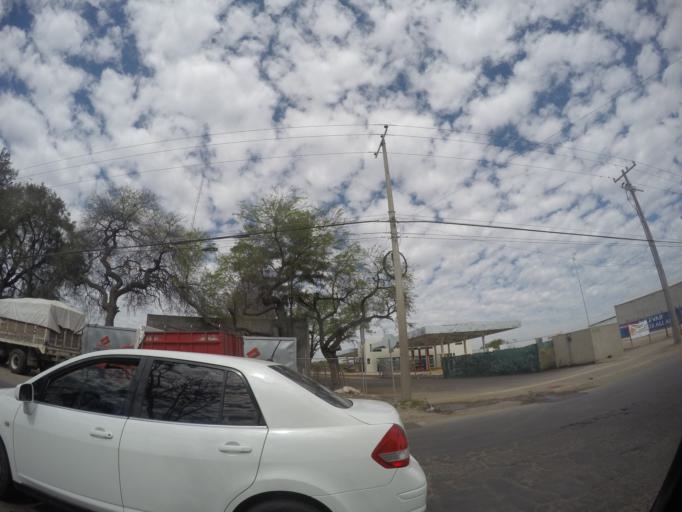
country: MX
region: Guanajuato
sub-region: Leon
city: San Jose de Duran (Los Troncoso)
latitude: 21.0790
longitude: -101.6807
